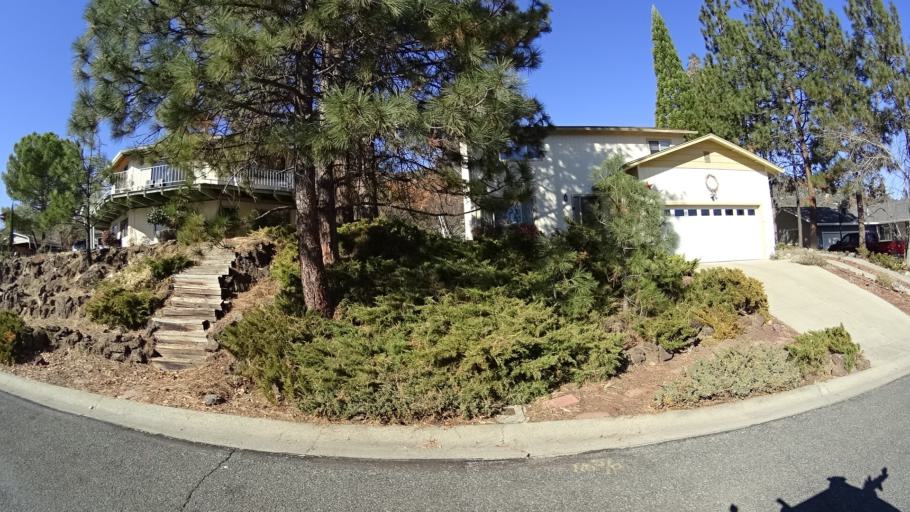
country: US
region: California
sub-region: Siskiyou County
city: Yreka
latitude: 41.7422
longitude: -122.6506
